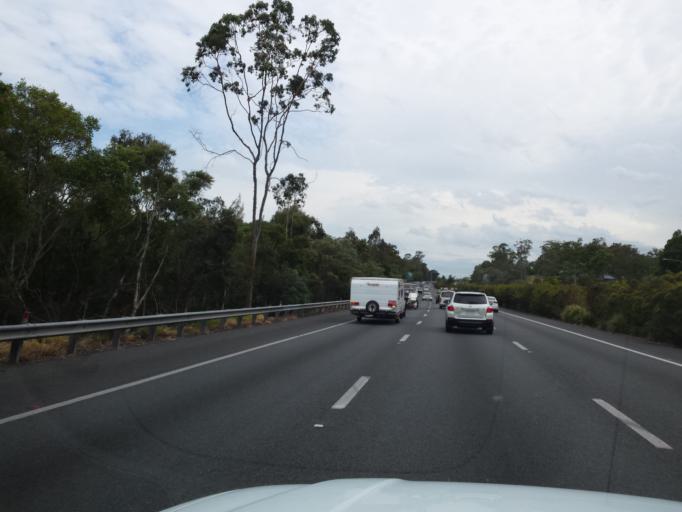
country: AU
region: Queensland
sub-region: Gold Coast
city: Nerang
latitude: -27.9636
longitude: 153.3458
